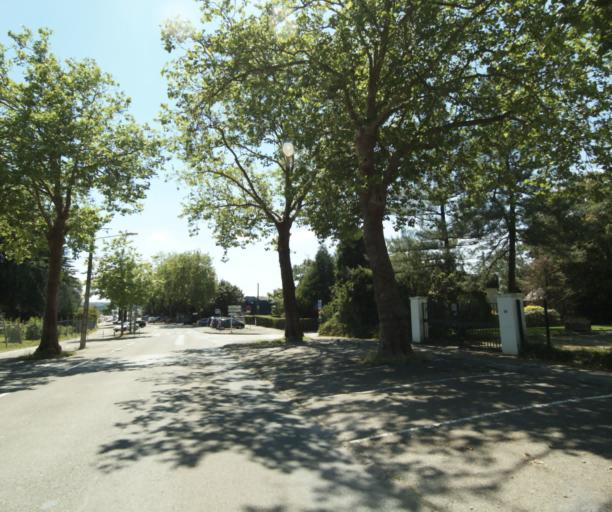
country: FR
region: Pays de la Loire
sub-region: Departement de la Mayenne
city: Laval
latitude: 48.0833
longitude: -0.7560
